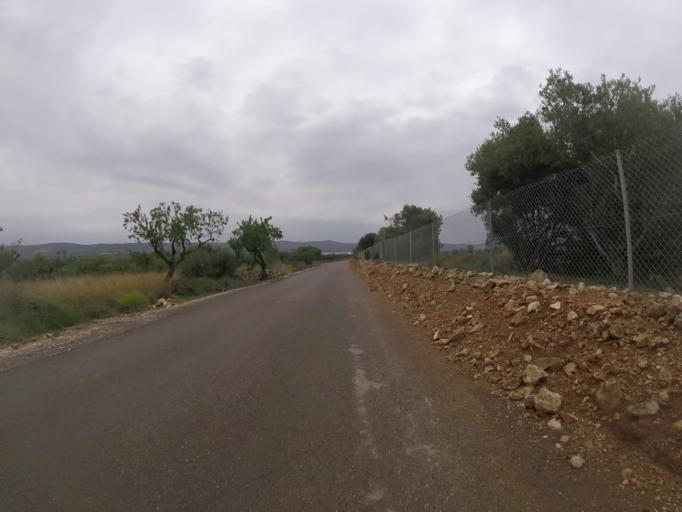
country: ES
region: Valencia
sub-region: Provincia de Castello
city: Alcala de Xivert
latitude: 40.2831
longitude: 0.2283
